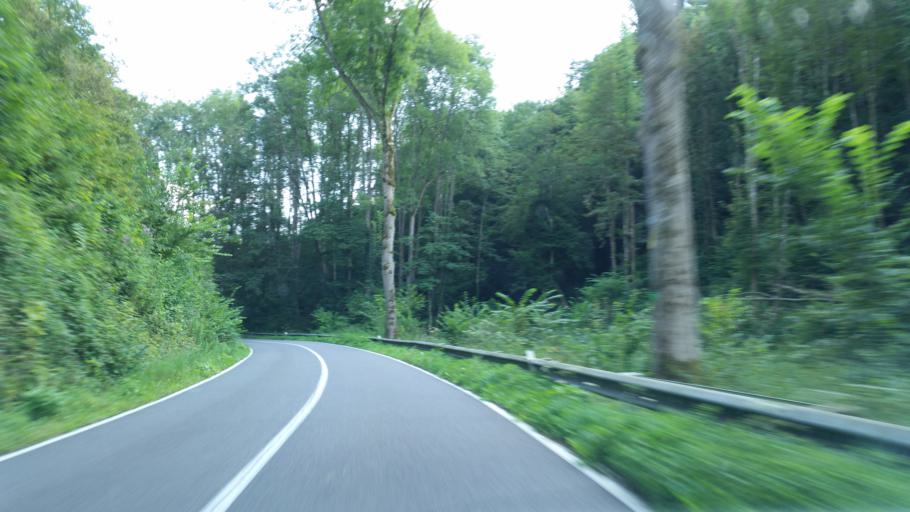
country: BE
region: Wallonia
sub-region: Province du Luxembourg
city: Durbuy
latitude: 50.3627
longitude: 5.4540
